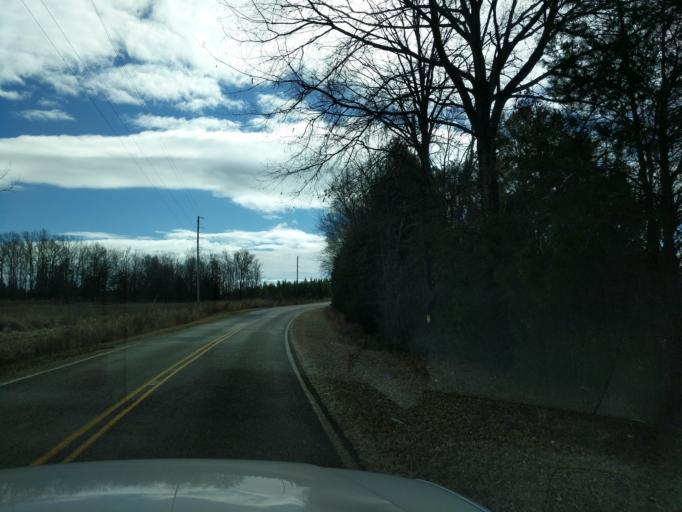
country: US
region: South Carolina
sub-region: Edgefield County
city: Edgefield
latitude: 33.9017
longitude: -82.0000
